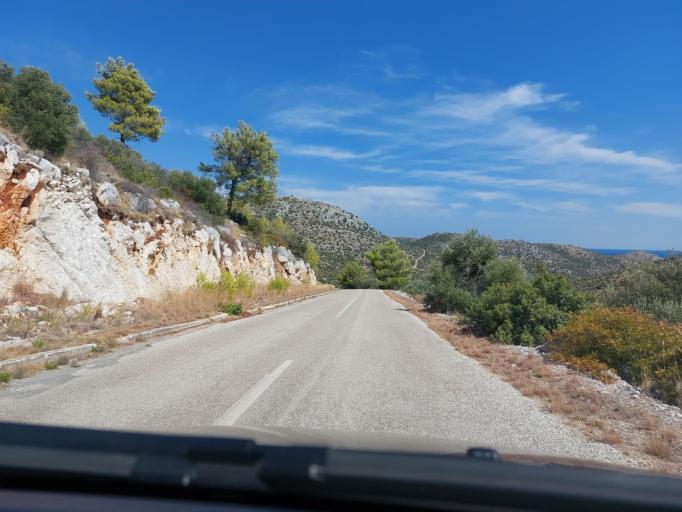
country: HR
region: Dubrovacko-Neretvanska
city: Smokvica
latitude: 42.7438
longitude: 16.8780
